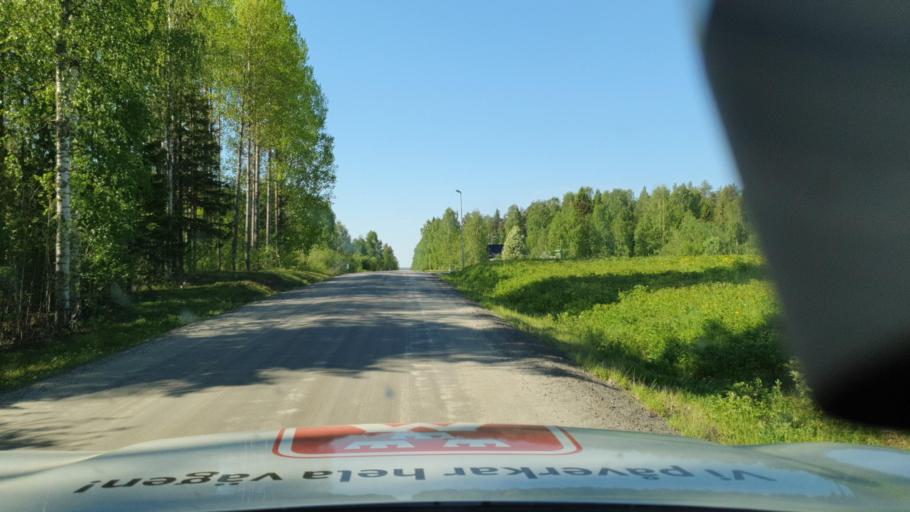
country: SE
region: Vaesterbotten
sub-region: Vannas Kommun
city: Vaennaes
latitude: 64.0162
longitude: 19.7461
